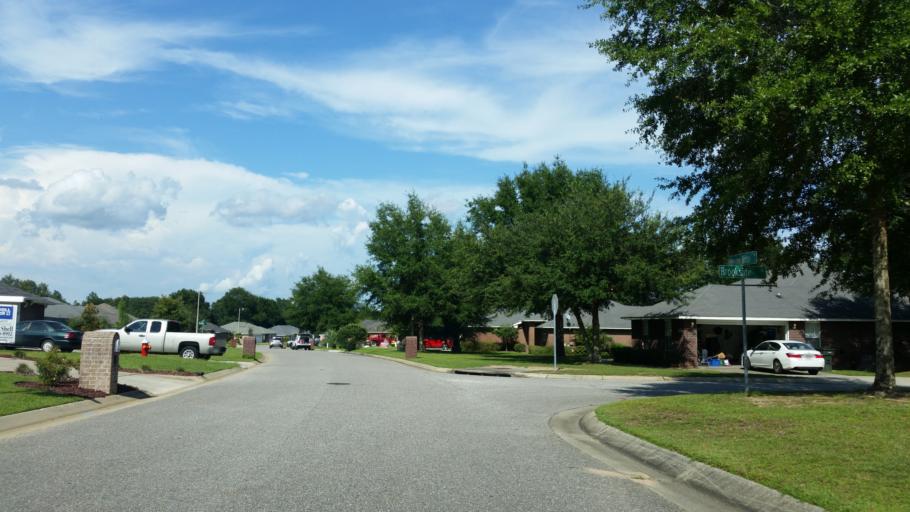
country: US
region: Florida
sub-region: Santa Rosa County
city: Pace
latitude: 30.6202
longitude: -87.1191
